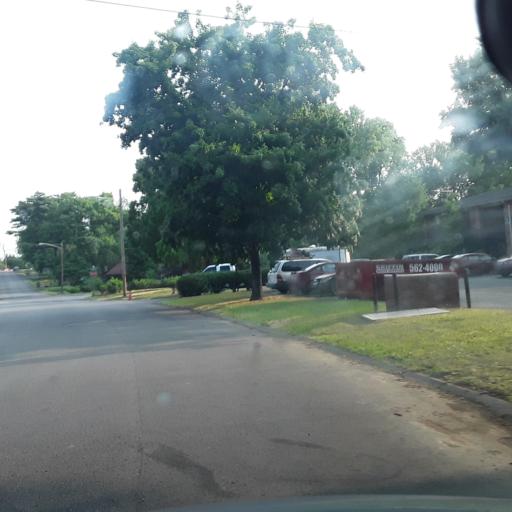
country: US
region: Tennessee
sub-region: Williamson County
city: Brentwood
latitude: 36.0575
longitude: -86.7192
